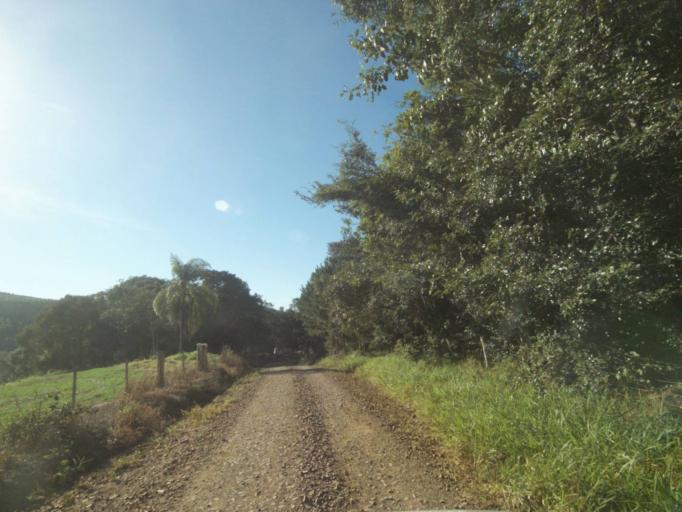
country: BR
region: Parana
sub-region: Tibagi
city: Tibagi
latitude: -24.5540
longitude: -50.5215
